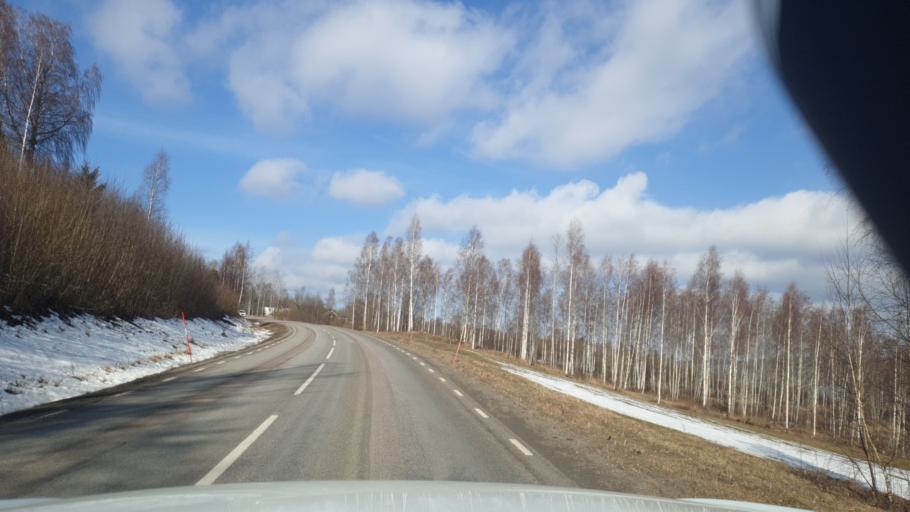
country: SE
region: Vaermland
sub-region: Eda Kommun
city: Amotfors
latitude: 59.6952
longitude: 12.3419
